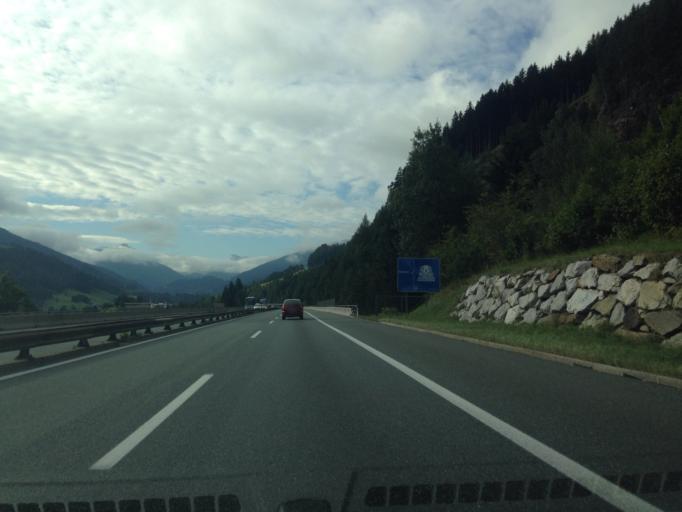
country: AT
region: Tyrol
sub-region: Politischer Bezirk Innsbruck Land
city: Matrei am Brenner
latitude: 47.1470
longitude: 11.4448
